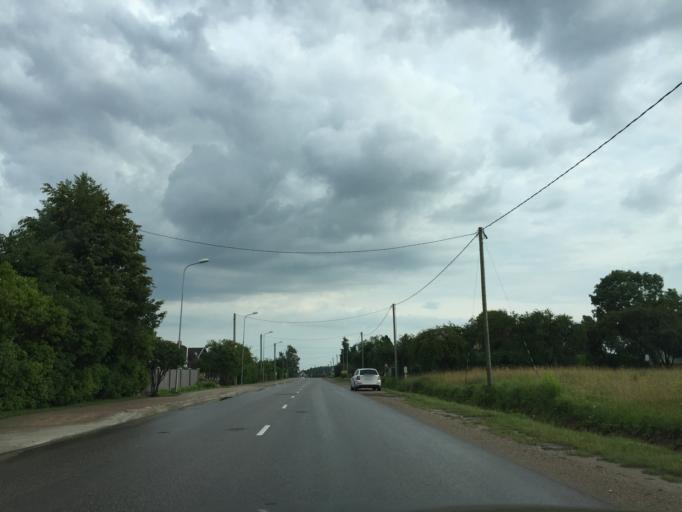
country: LV
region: Dobeles Rajons
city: Dobele
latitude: 56.6130
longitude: 23.2735
